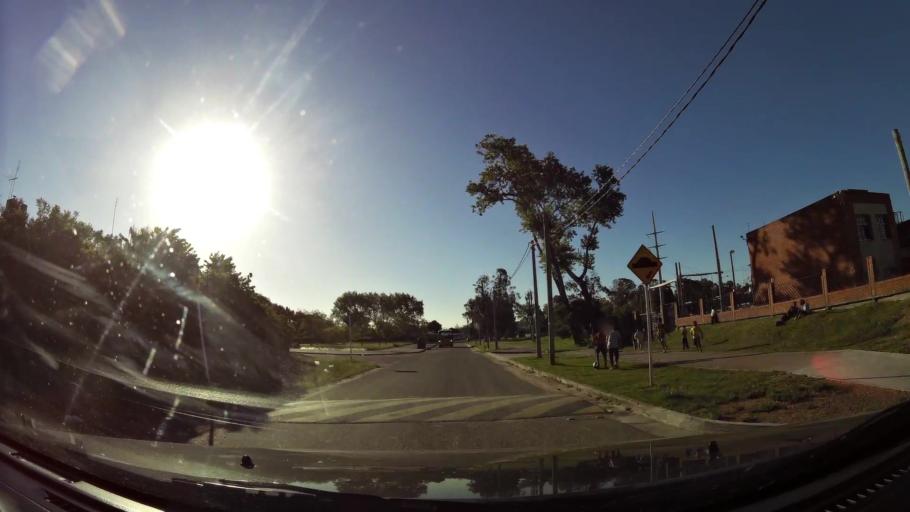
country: UY
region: Canelones
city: Paso de Carrasco
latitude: -34.8694
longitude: -56.0581
